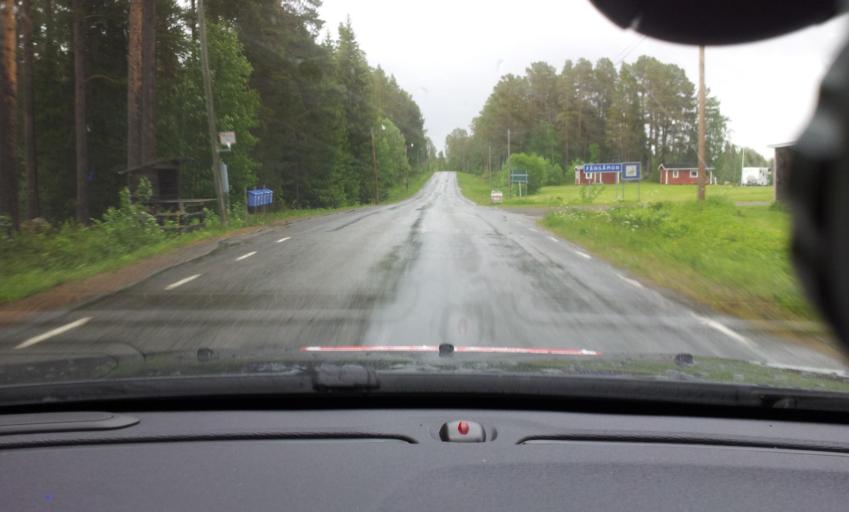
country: SE
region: Jaemtland
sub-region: Are Kommun
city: Are
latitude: 63.1837
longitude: 13.1212
